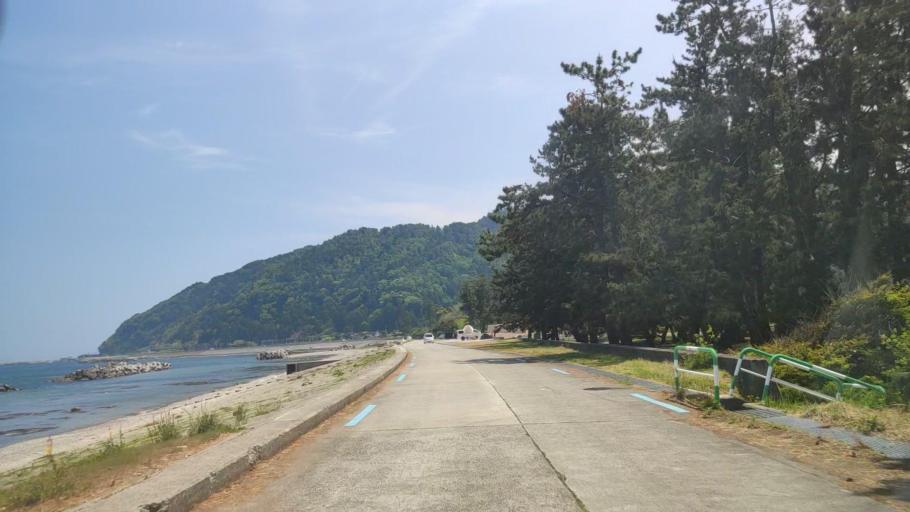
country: JP
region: Toyama
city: Nyuzen
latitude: 36.9630
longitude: 137.5693
